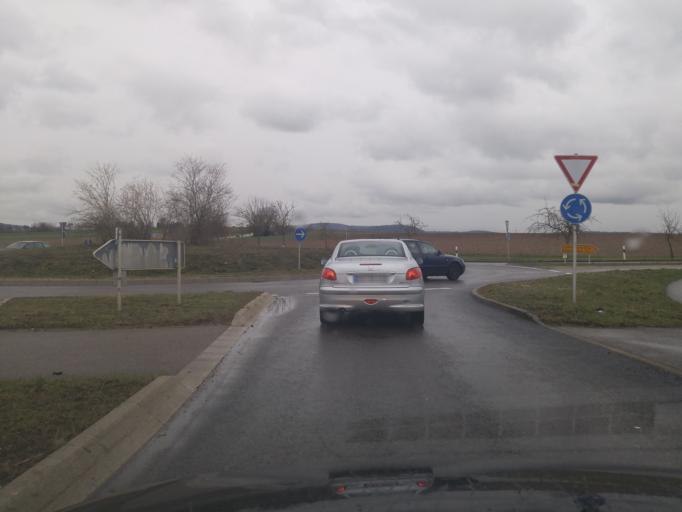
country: DE
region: Baden-Wuerttemberg
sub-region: Regierungsbezirk Stuttgart
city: Schwaikheim
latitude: 48.8928
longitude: 9.3633
